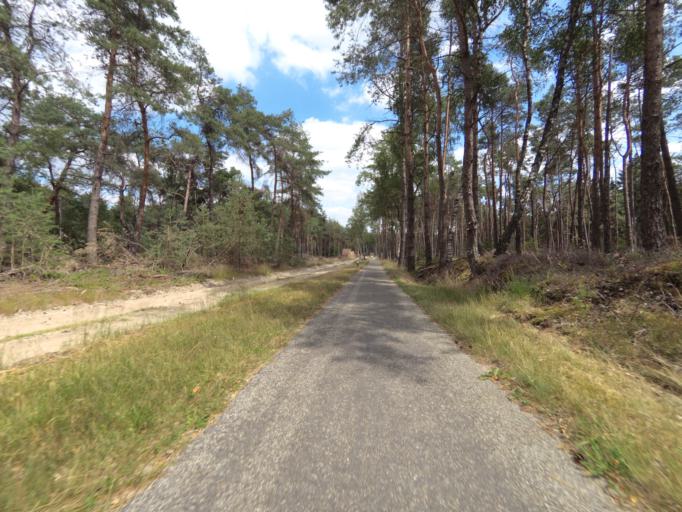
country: NL
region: Overijssel
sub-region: Gemeente Hof van Twente
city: Markelo
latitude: 52.3174
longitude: 6.4393
